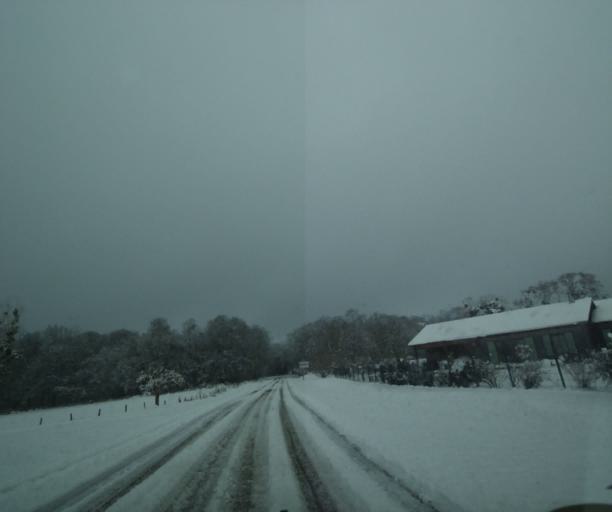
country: FR
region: Champagne-Ardenne
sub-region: Departement de la Haute-Marne
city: Montier-en-Der
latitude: 48.5376
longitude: 4.8095
